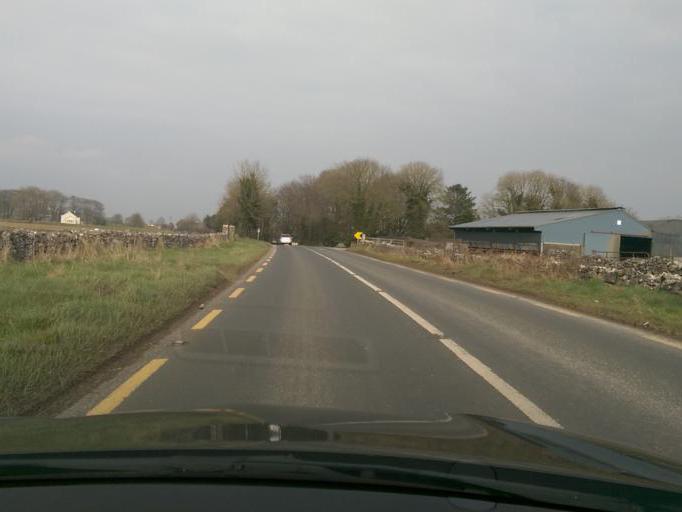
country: IE
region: Connaught
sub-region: Roscommon
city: Roscommon
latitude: 53.5943
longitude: -8.2166
